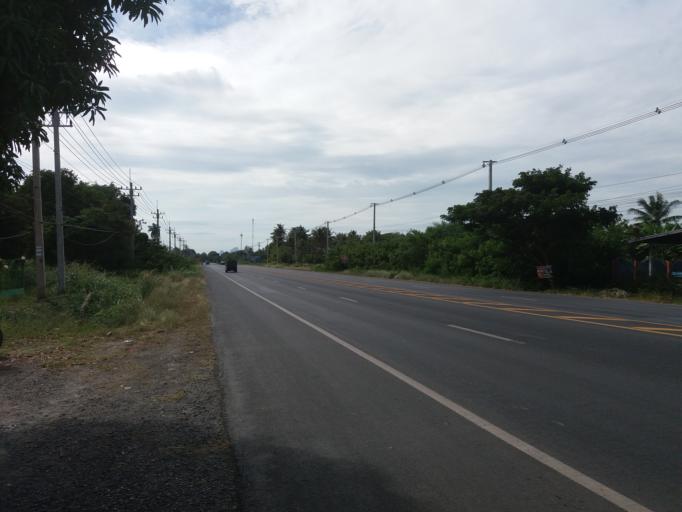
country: TH
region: Lop Buri
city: Phatthana Nikhom
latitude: 14.8404
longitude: 100.8617
